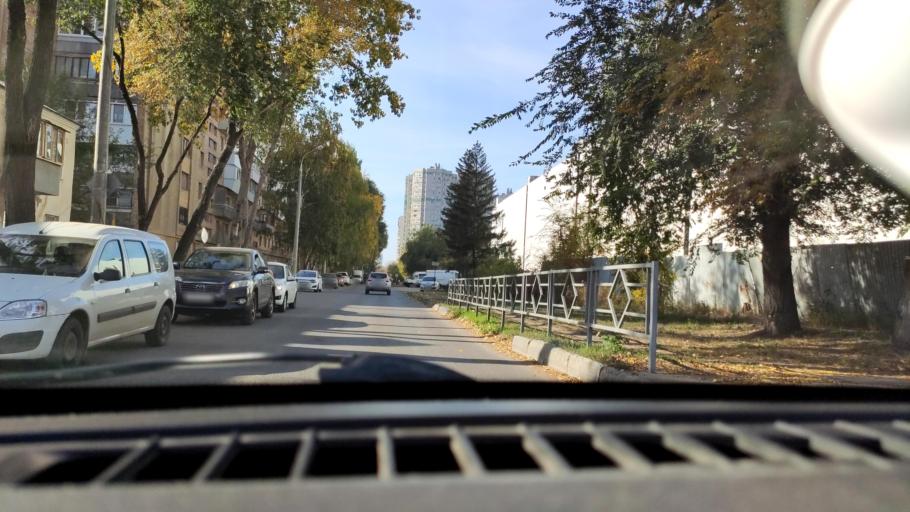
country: RU
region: Samara
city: Samara
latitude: 53.2041
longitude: 50.1902
